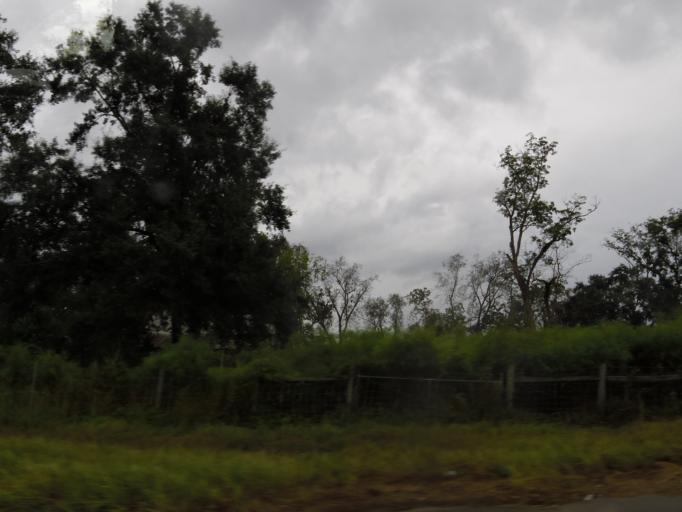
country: US
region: Georgia
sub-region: Wayne County
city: Jesup
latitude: 31.5597
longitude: -81.8306
